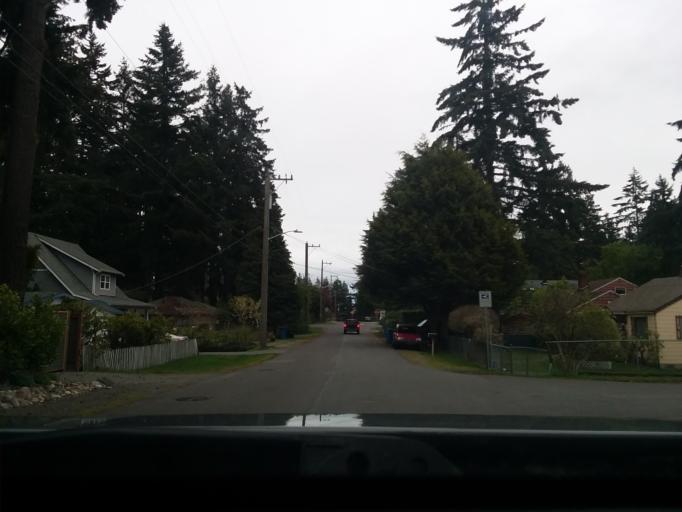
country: US
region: Washington
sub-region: King County
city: Shoreline
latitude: 47.7359
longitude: -122.3532
